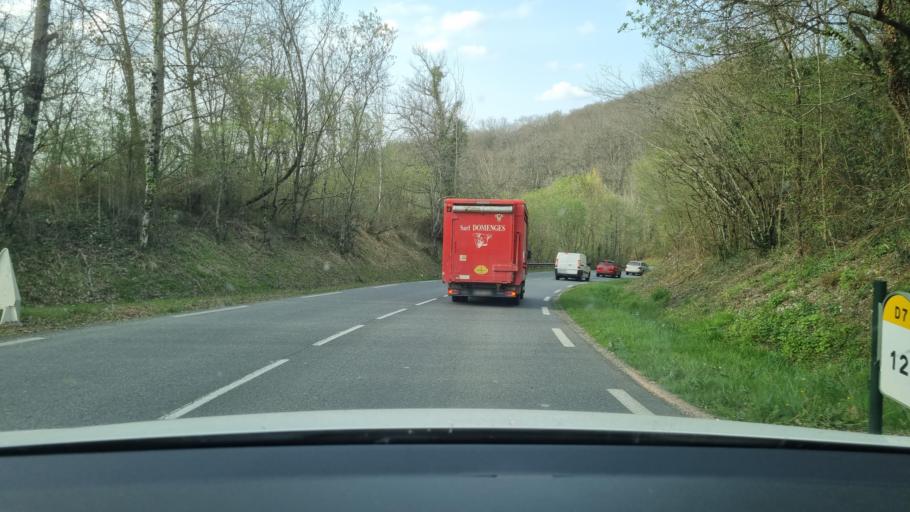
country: FR
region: Aquitaine
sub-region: Departement des Pyrenees-Atlantiques
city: Soumoulou
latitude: 43.3747
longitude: -0.1078
